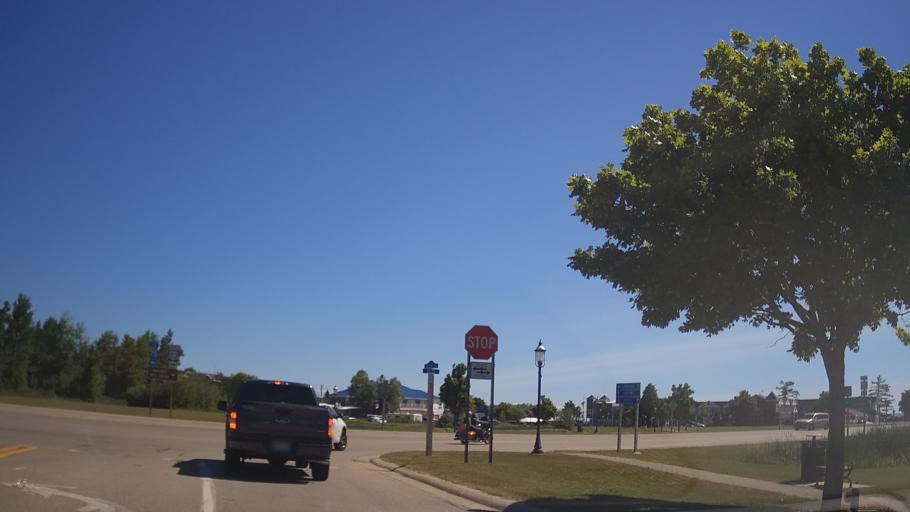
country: US
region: Michigan
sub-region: Mackinac County
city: Saint Ignace
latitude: 45.7710
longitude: -84.7295
